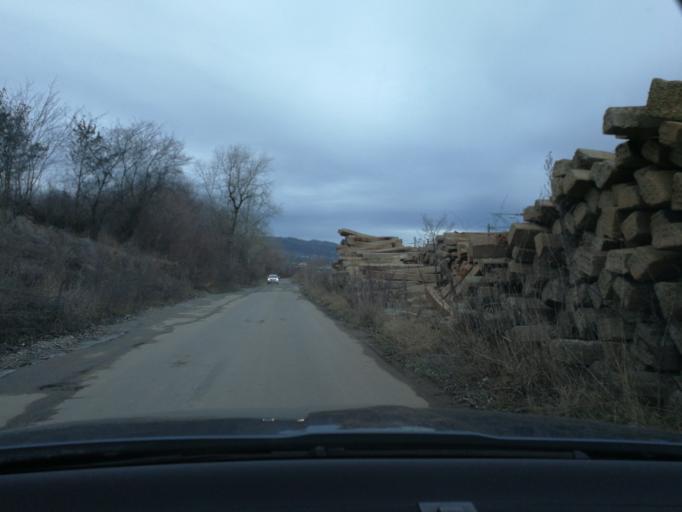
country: RO
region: Prahova
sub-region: Comuna Cornu
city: Cornu de Jos
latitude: 45.1378
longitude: 25.7020
